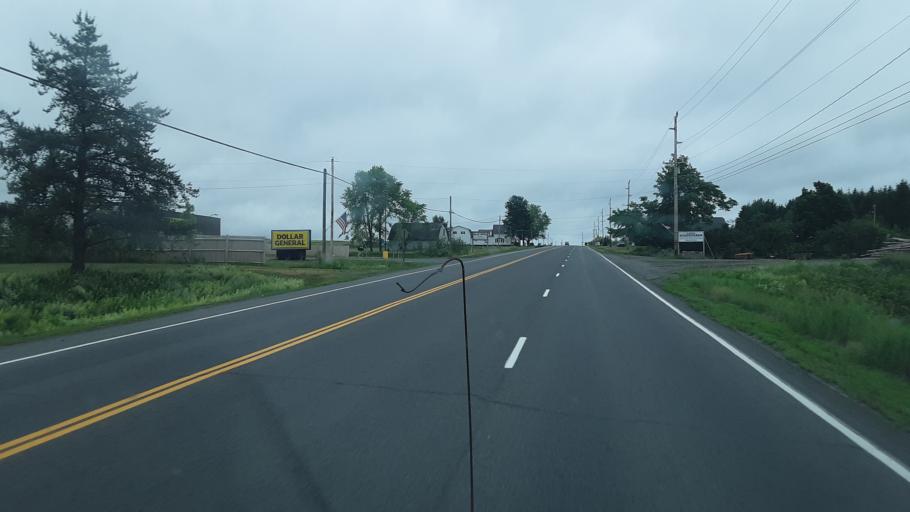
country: US
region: Maine
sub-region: Penobscot County
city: Patten
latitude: 45.9855
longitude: -68.4497
